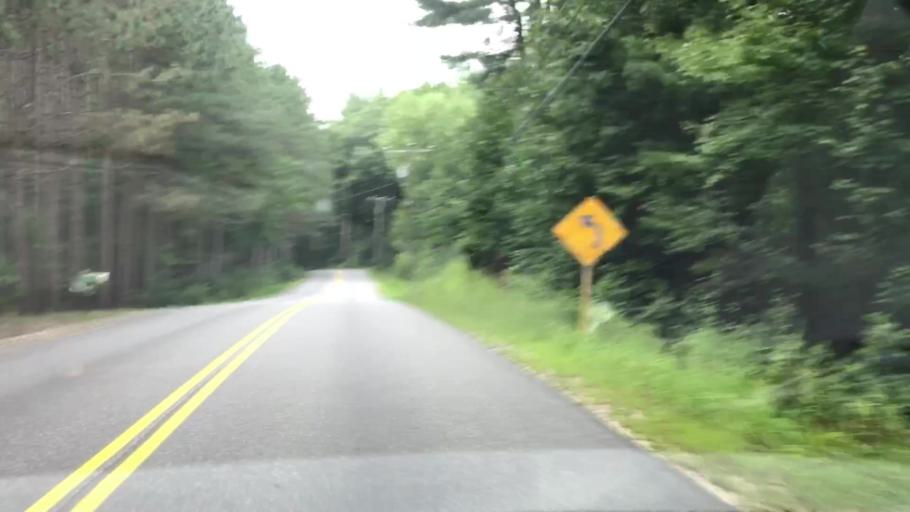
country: US
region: New Hampshire
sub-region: Hillsborough County
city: Milford
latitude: 42.8230
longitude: -71.6012
